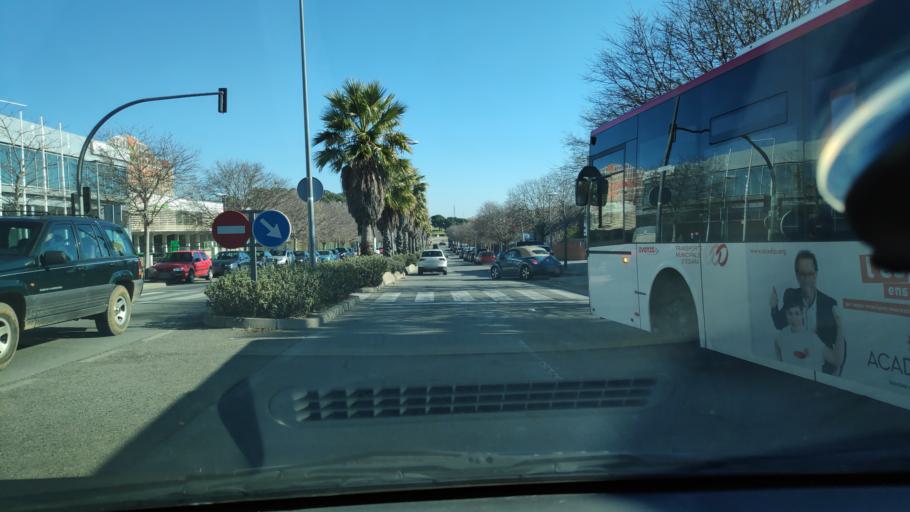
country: ES
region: Catalonia
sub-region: Provincia de Barcelona
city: Terrassa
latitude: 41.5577
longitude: 2.0356
